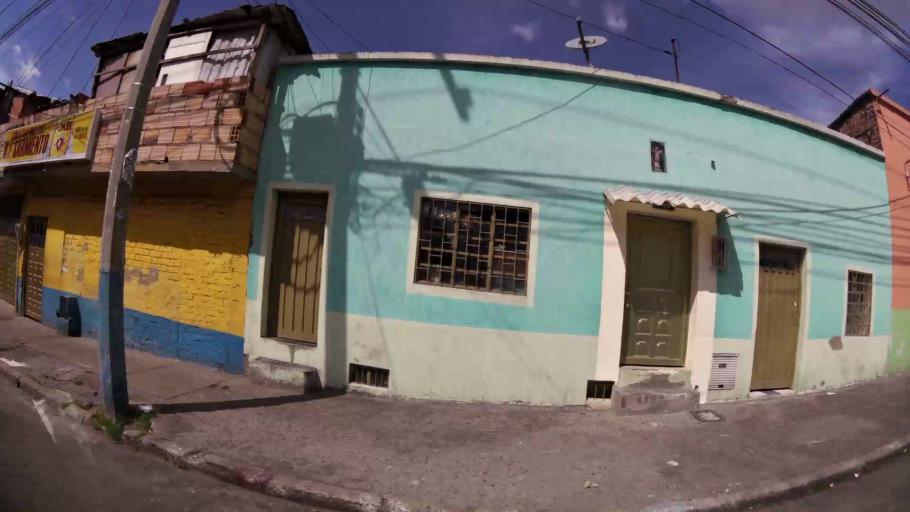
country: CO
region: Bogota D.C.
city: Bogota
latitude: 4.5658
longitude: -74.1006
